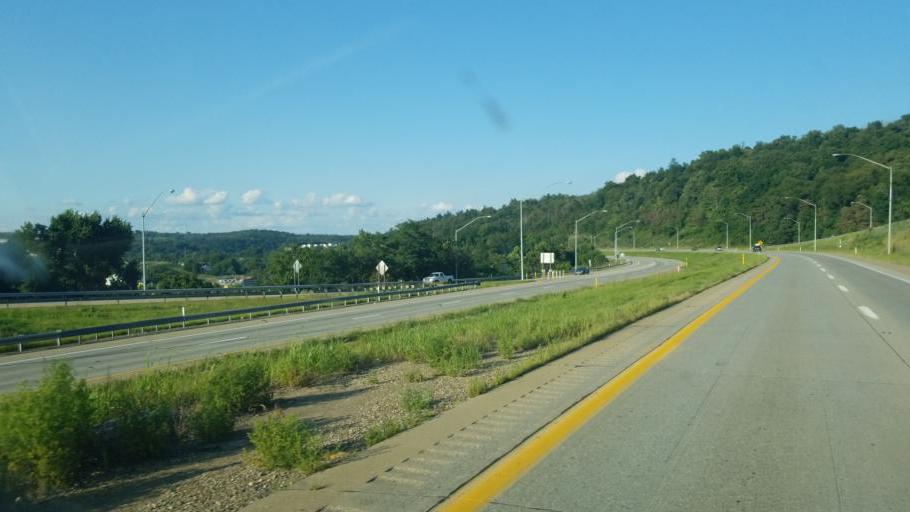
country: US
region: Pennsylvania
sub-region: Washington County
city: Canonsburg
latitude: 40.2643
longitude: -80.1669
